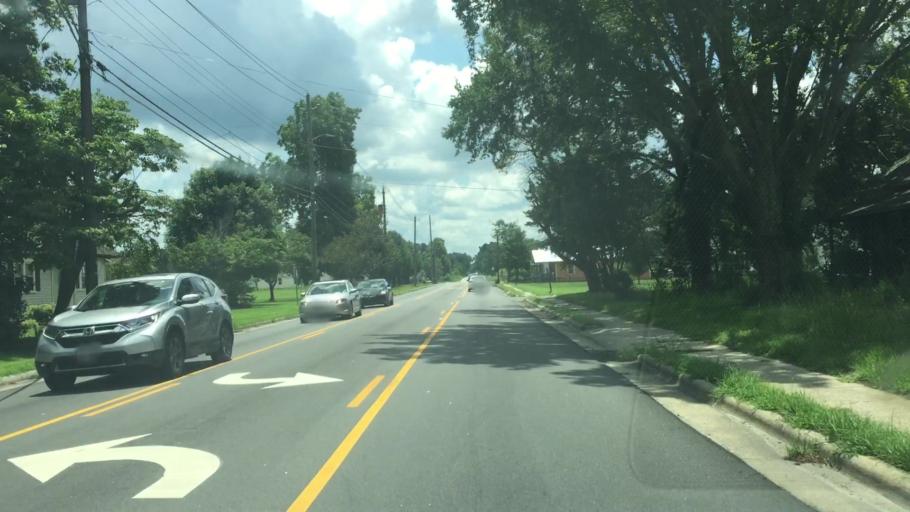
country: US
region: North Carolina
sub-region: Columbus County
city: Chadbourn
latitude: 34.3183
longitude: -78.8264
